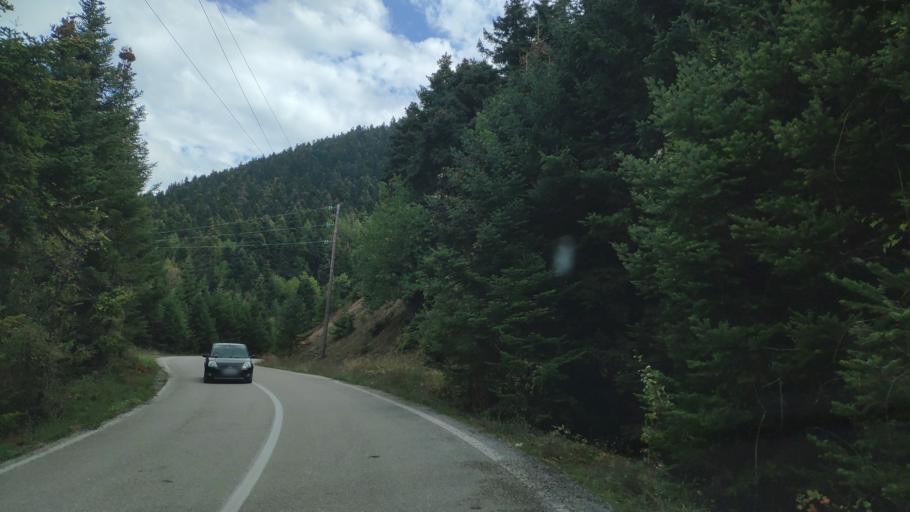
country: GR
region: Central Greece
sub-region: Nomos Fthiotidos
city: Stavros
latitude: 38.7306
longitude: 22.3532
